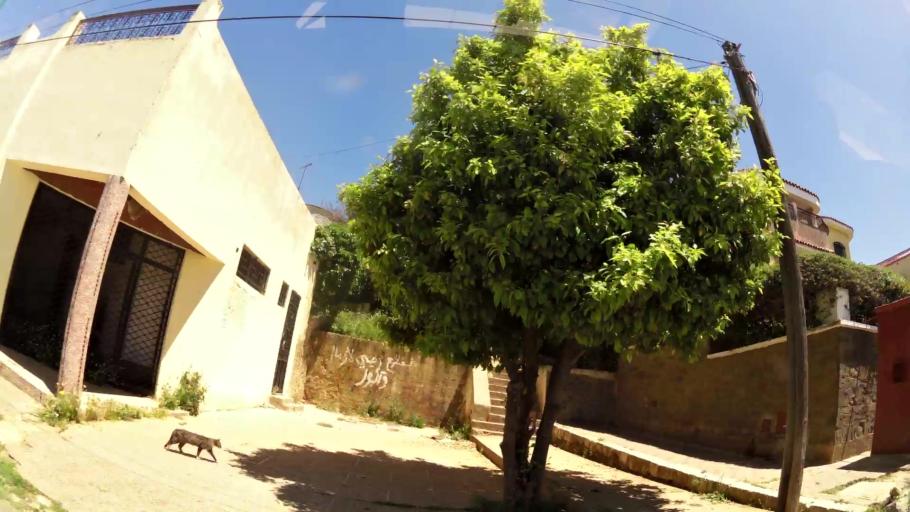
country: MA
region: Meknes-Tafilalet
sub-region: Meknes
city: Meknes
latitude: 33.9071
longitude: -5.5619
